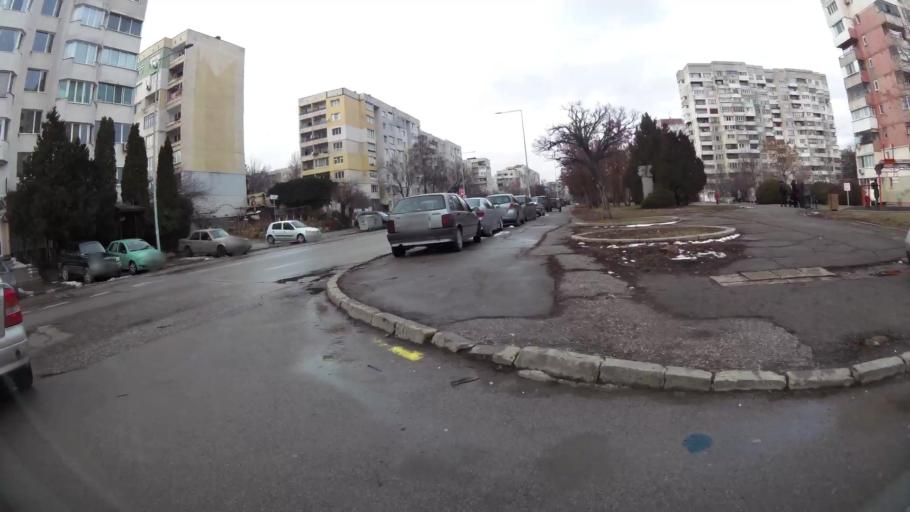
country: BG
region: Sofiya
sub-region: Obshtina Bozhurishte
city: Bozhurishte
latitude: 42.7134
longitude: 23.2473
